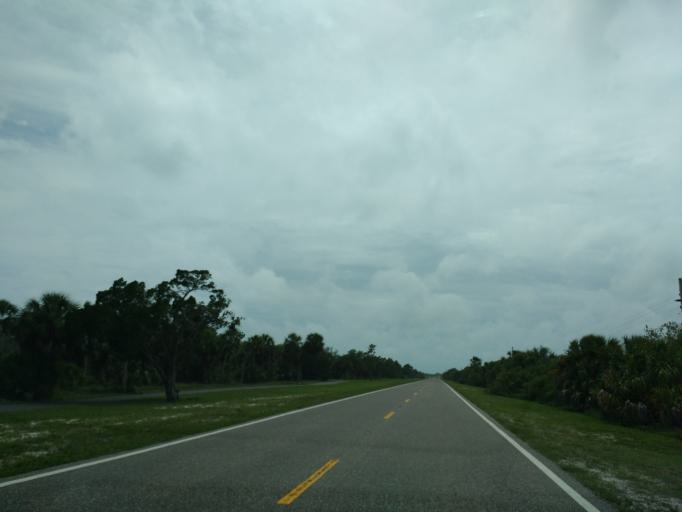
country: US
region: Florida
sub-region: Pinellas County
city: Tierra Verde
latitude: 27.6209
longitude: -82.7202
